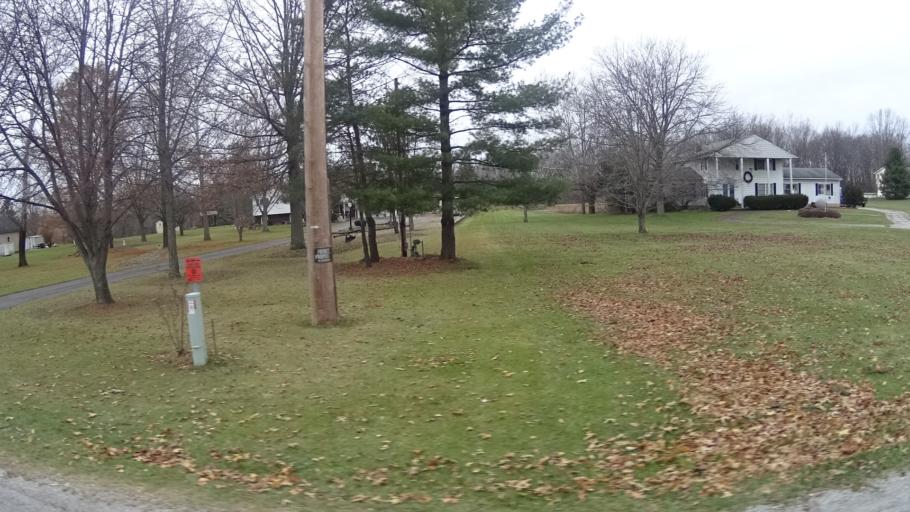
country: US
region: Ohio
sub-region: Lorain County
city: Wellington
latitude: 41.1727
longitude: -82.1934
